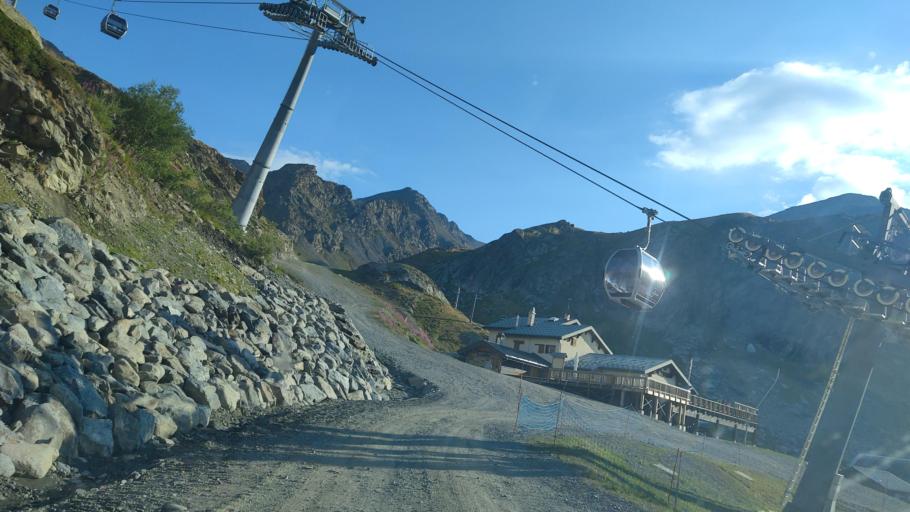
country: FR
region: Rhone-Alpes
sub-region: Departement de la Savoie
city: Val Thorens
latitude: 45.2463
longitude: 6.5692
